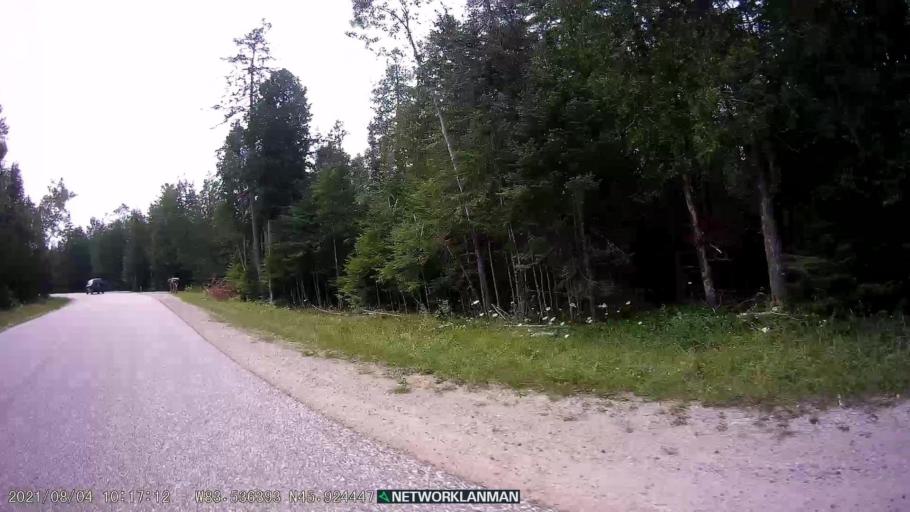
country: CA
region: Ontario
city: Thessalon
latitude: 45.9243
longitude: -83.5365
